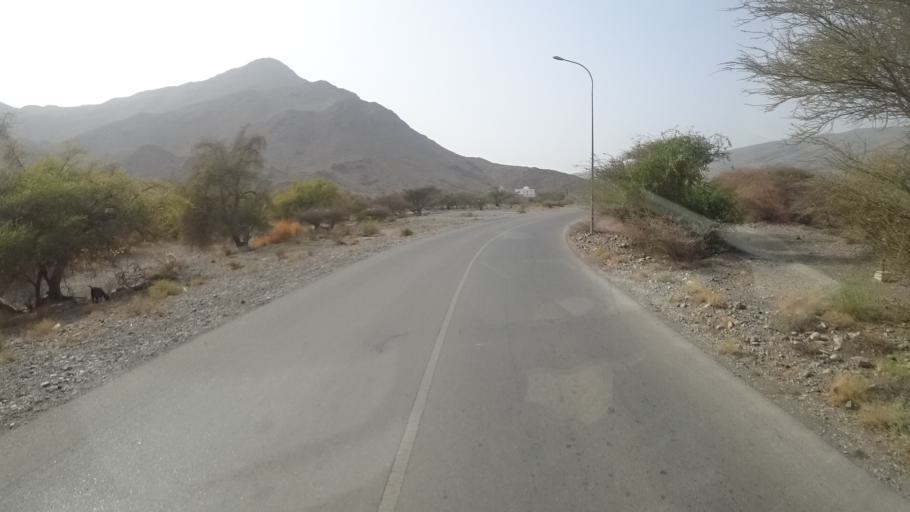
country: OM
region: Muhafazat ad Dakhiliyah
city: Bahla'
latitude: 23.0482
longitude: 57.4261
